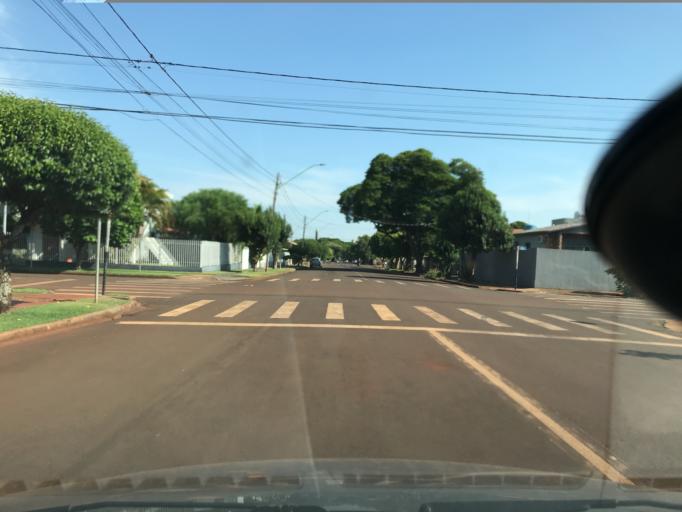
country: BR
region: Parana
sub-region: Palotina
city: Palotina
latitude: -24.2893
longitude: -53.8406
